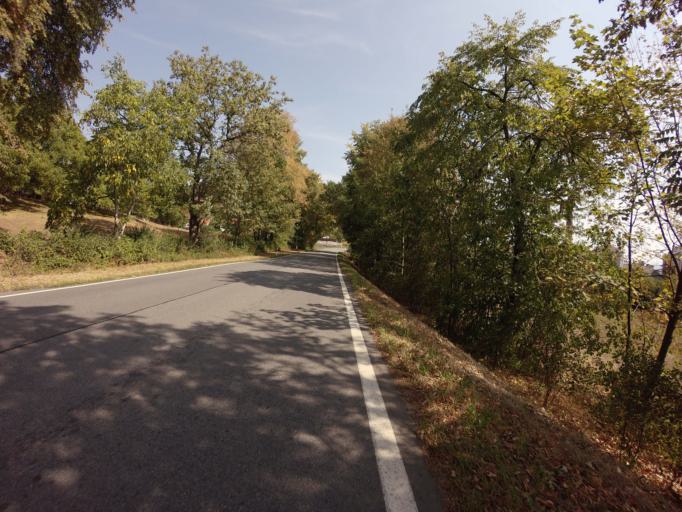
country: CZ
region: Central Bohemia
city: Sedlcany
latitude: 49.6142
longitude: 14.3899
